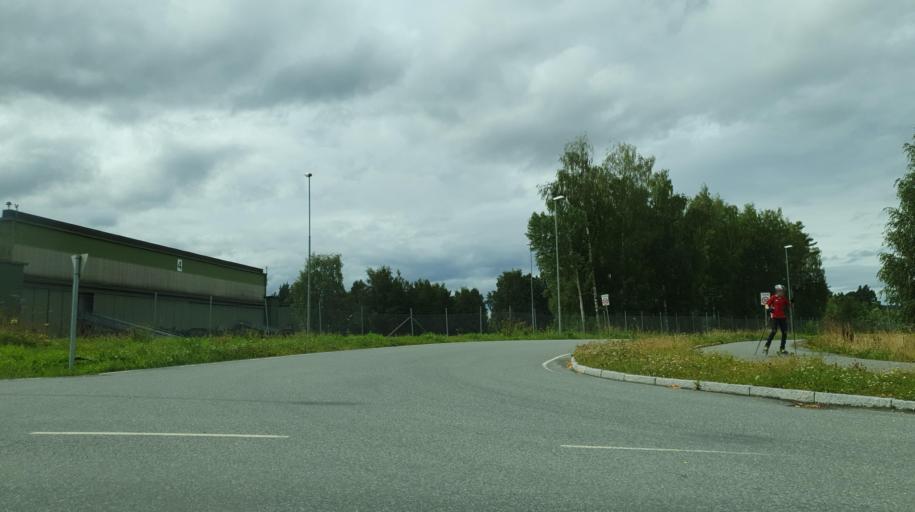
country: NO
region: Nord-Trondelag
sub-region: Stjordal
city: Stjordalshalsen
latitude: 63.4648
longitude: 10.9399
